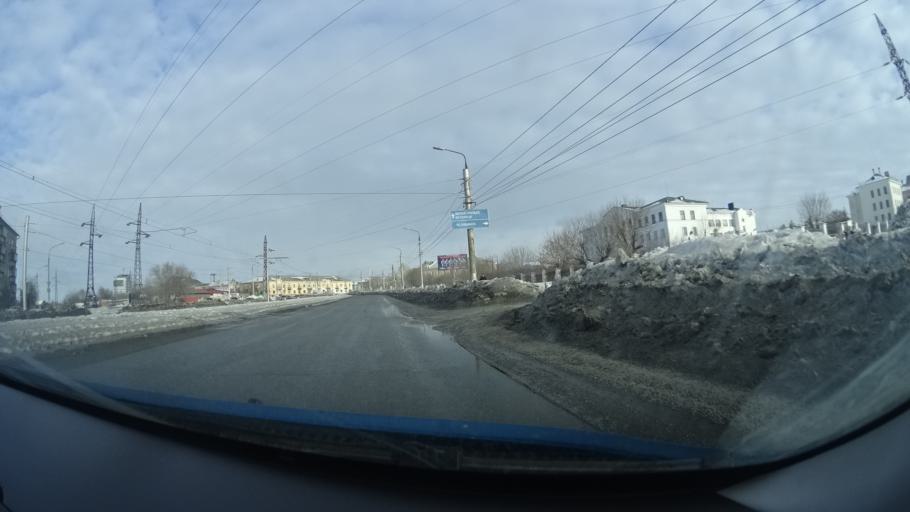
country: RU
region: Chelyabinsk
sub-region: Gorod Magnitogorsk
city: Magnitogorsk
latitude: 53.4344
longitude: 58.9878
